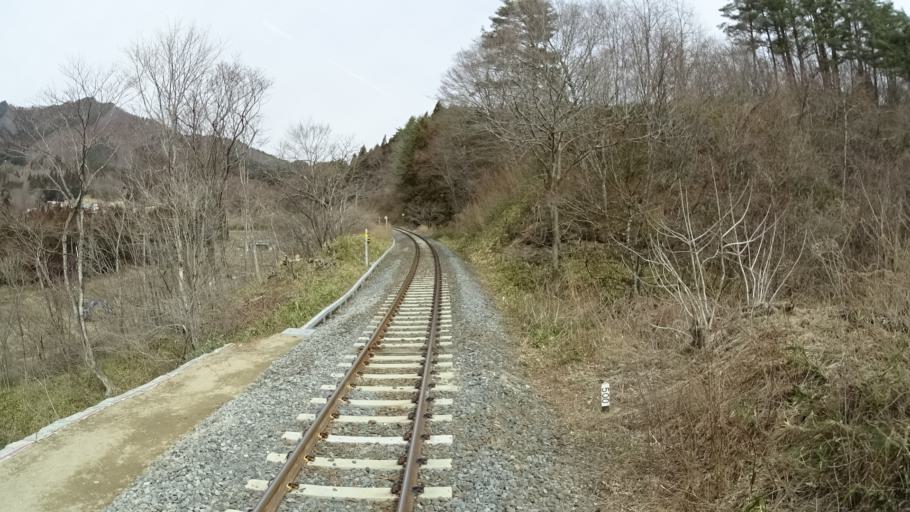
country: JP
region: Iwate
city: Yamada
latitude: 39.4858
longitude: 141.9251
